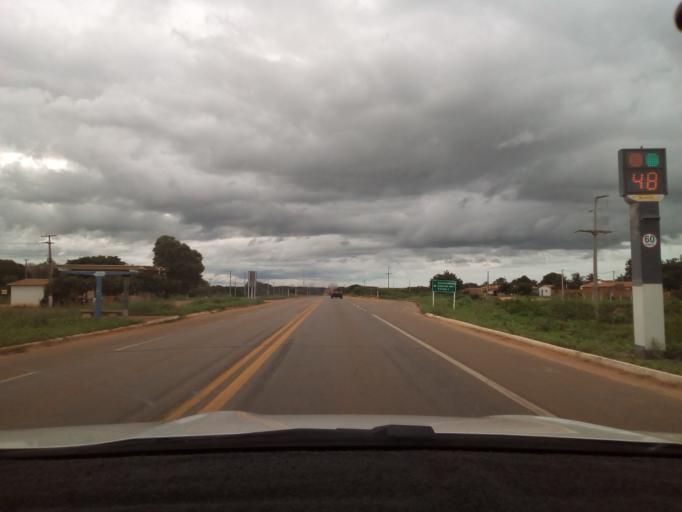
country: BR
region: Rio Grande do Norte
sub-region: Mossoro
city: Mossoro
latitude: -4.9458
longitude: -37.4054
